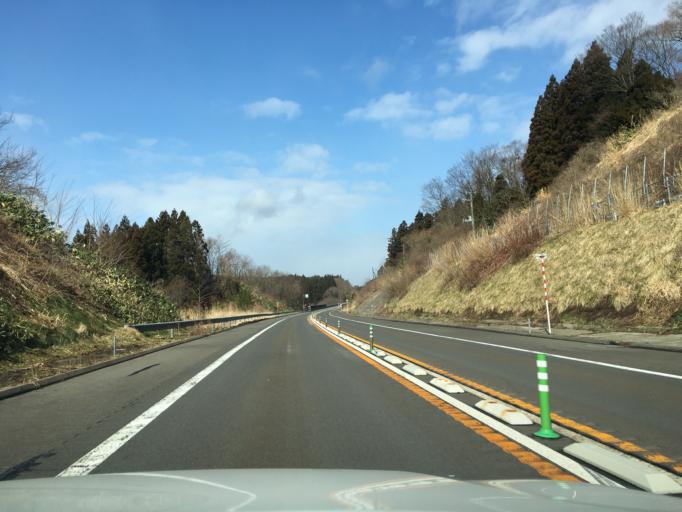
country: JP
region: Akita
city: Akita
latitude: 39.7430
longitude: 140.1628
